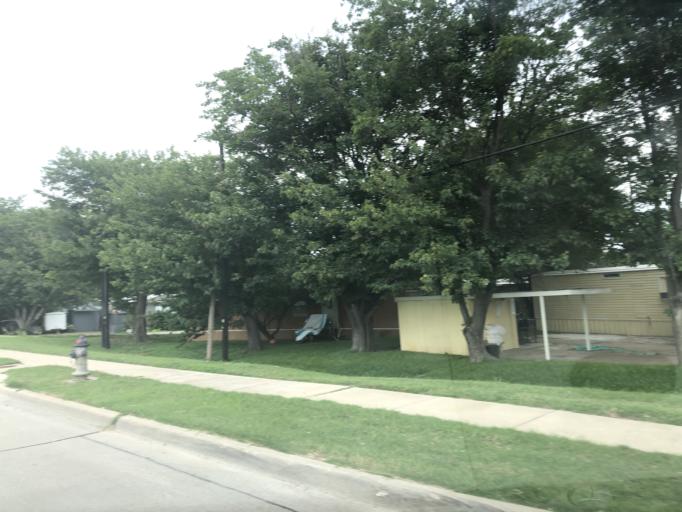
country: US
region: Texas
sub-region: Dallas County
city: Irving
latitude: 32.7830
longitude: -96.9718
